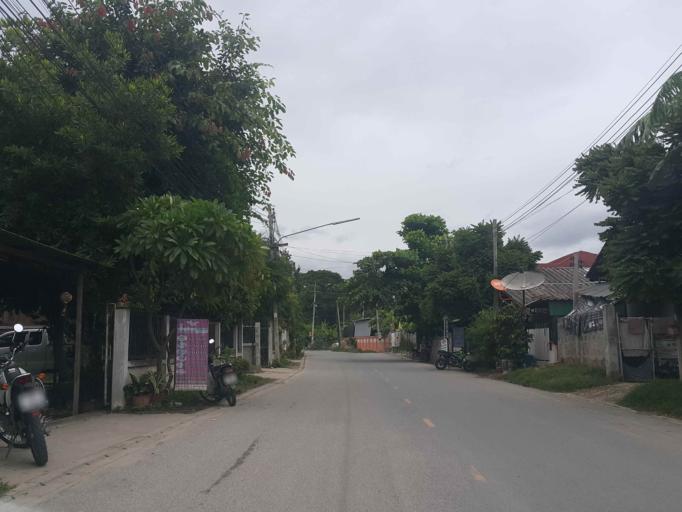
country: TH
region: Chiang Mai
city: Chiang Mai
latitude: 18.7528
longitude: 98.9870
